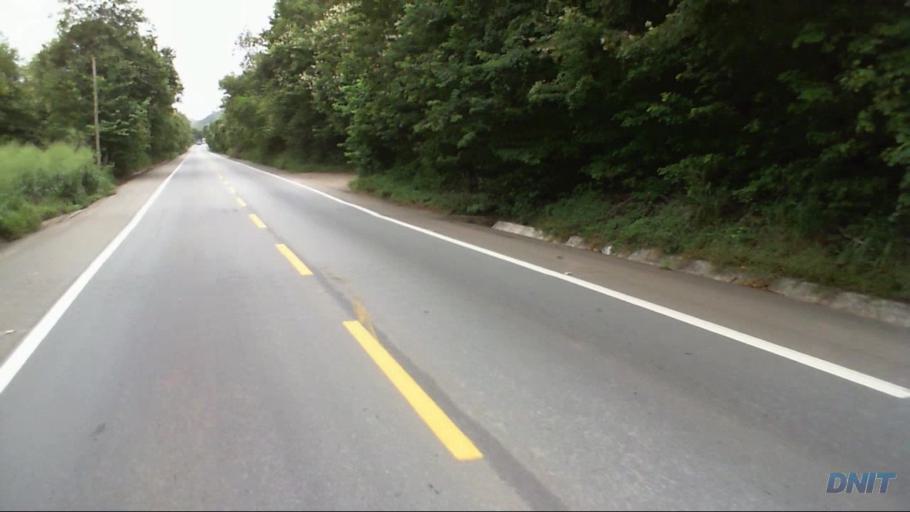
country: BR
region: Minas Gerais
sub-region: Timoteo
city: Timoteo
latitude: -19.5521
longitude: -42.7058
